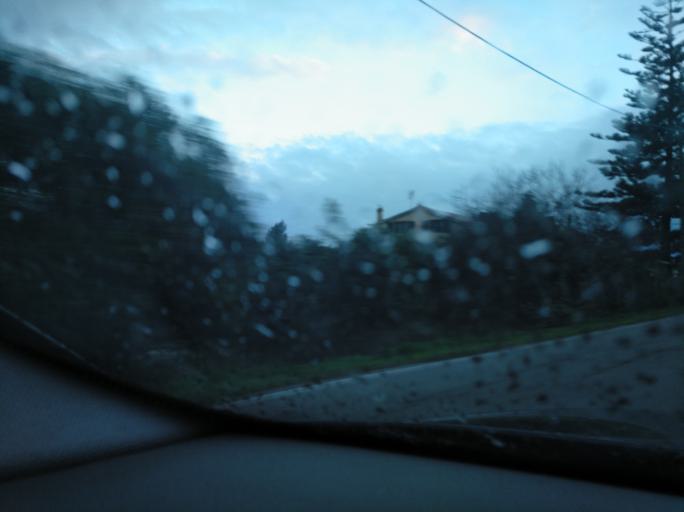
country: PT
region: Faro
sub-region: Vila Real de Santo Antonio
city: Monte Gordo
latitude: 37.1913
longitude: -7.4842
